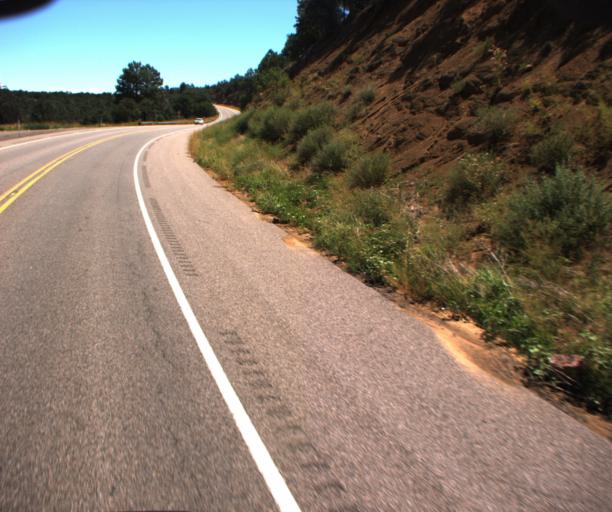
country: US
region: Arizona
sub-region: Navajo County
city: Cibecue
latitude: 33.6936
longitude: -110.5666
